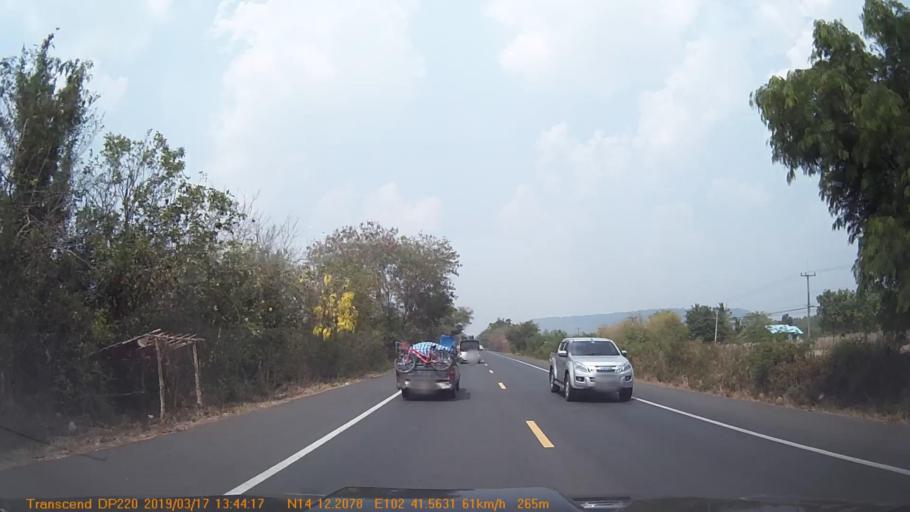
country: TH
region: Buriram
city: Non Din Daeng
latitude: 14.2038
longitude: 102.6928
